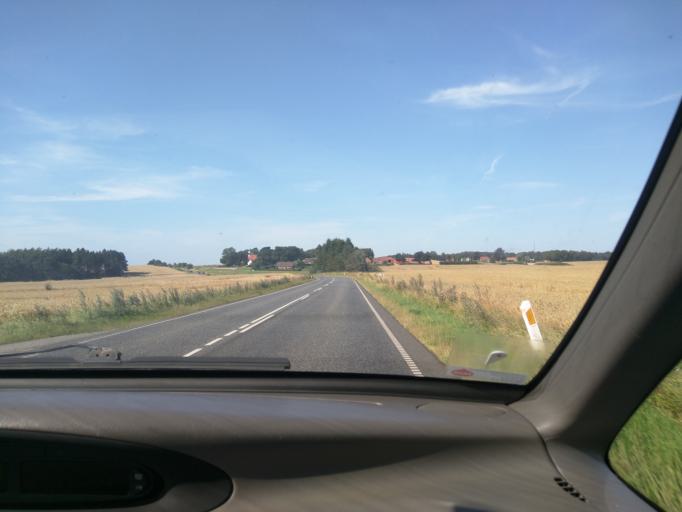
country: DK
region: Central Jutland
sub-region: Viborg Kommune
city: Bjerringbro
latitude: 56.3465
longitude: 9.6803
